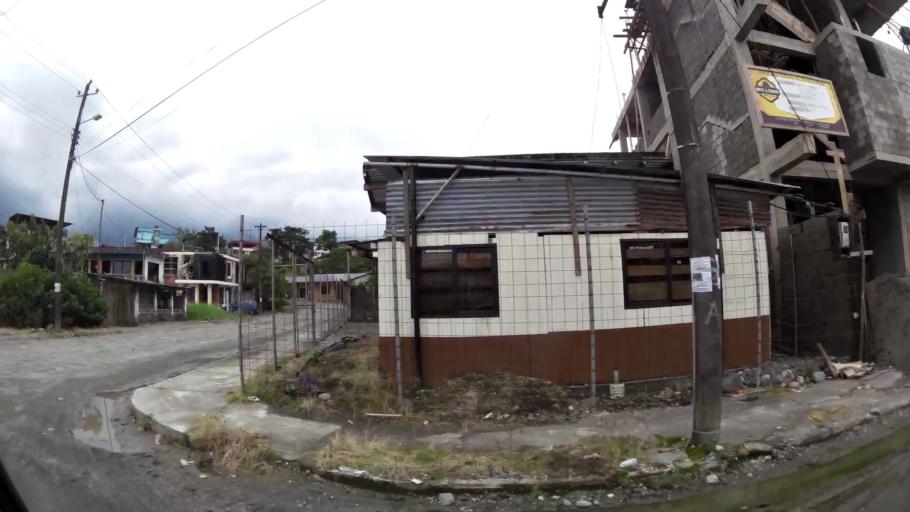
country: EC
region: Pastaza
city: Puyo
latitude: -1.4921
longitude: -78.0072
